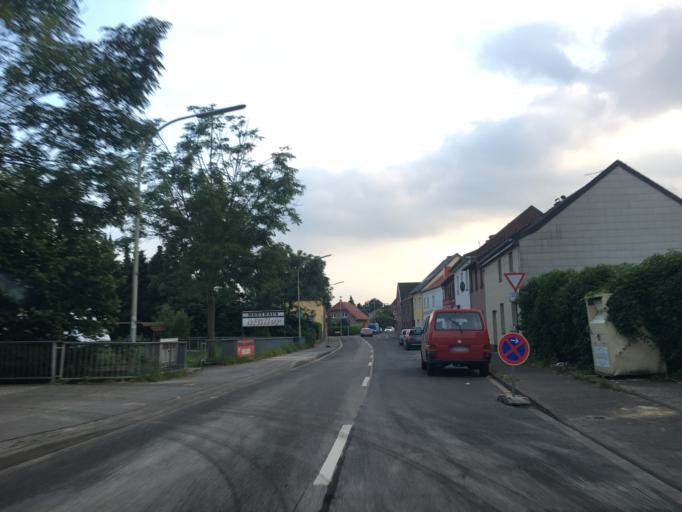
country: DE
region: North Rhine-Westphalia
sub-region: Regierungsbezirk Koln
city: Wassenberg
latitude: 51.0723
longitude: 6.1848
